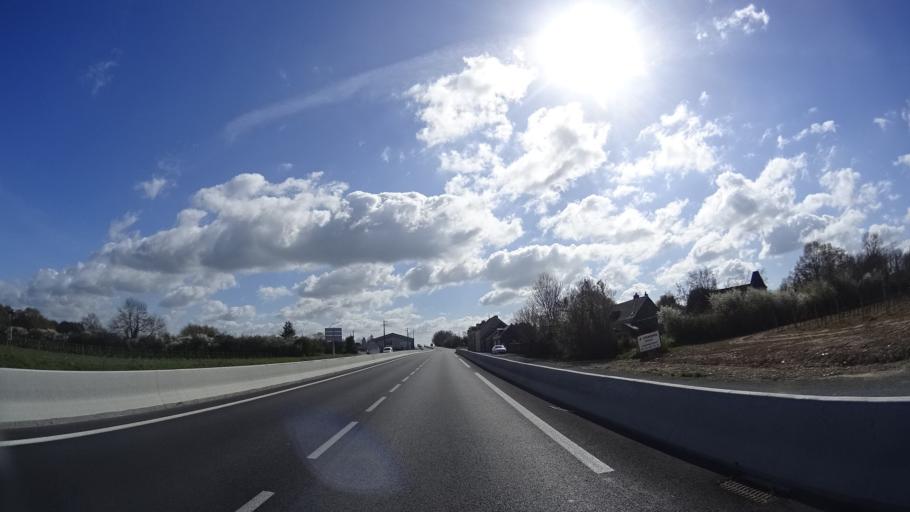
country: FR
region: Pays de la Loire
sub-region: Departement de Maine-et-Loire
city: Saint-Melaine-sur-Aubance
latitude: 47.3886
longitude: -0.4961
